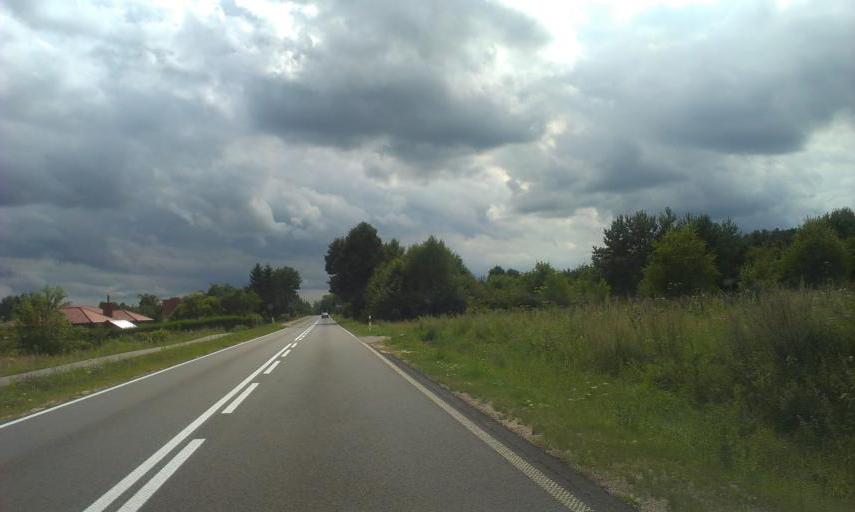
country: PL
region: West Pomeranian Voivodeship
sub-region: Koszalin
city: Koszalin
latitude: 54.0735
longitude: 16.1627
